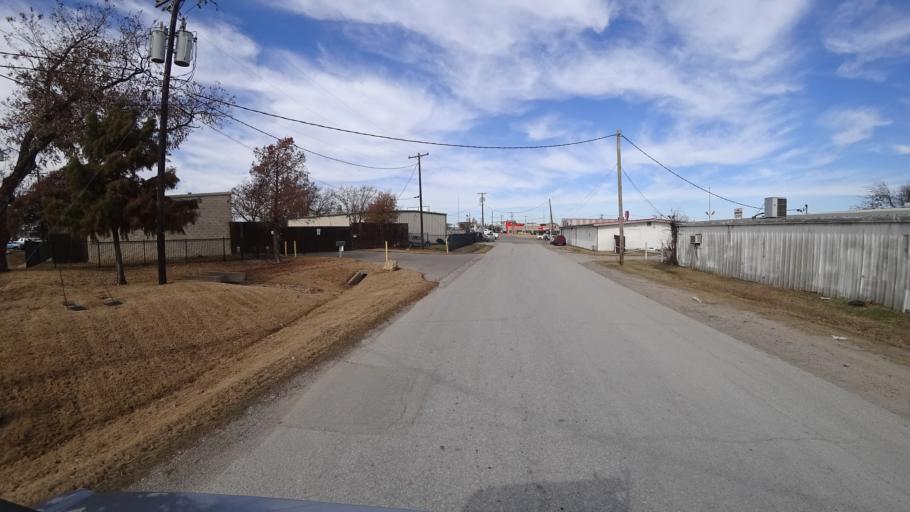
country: US
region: Texas
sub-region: Denton County
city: Lewisville
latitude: 33.0420
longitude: -96.9805
